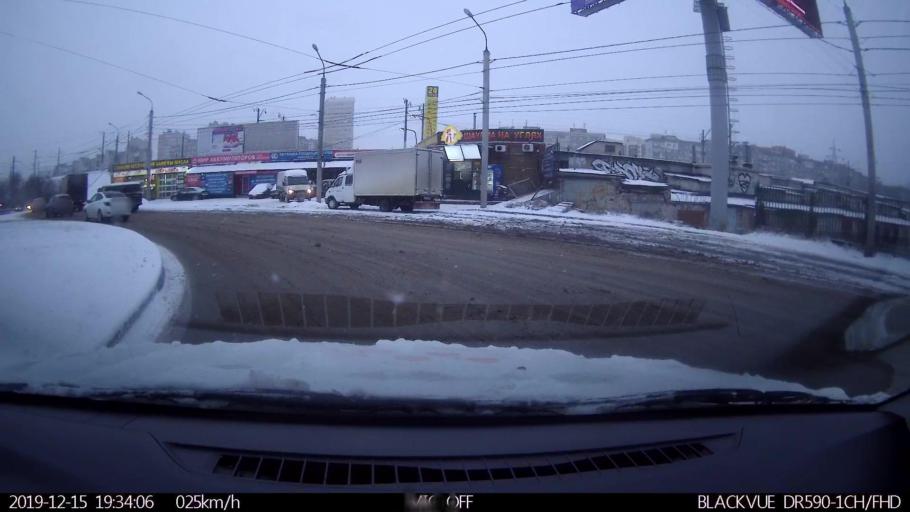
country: RU
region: Nizjnij Novgorod
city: Nizhniy Novgorod
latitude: 56.3384
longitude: 43.9216
